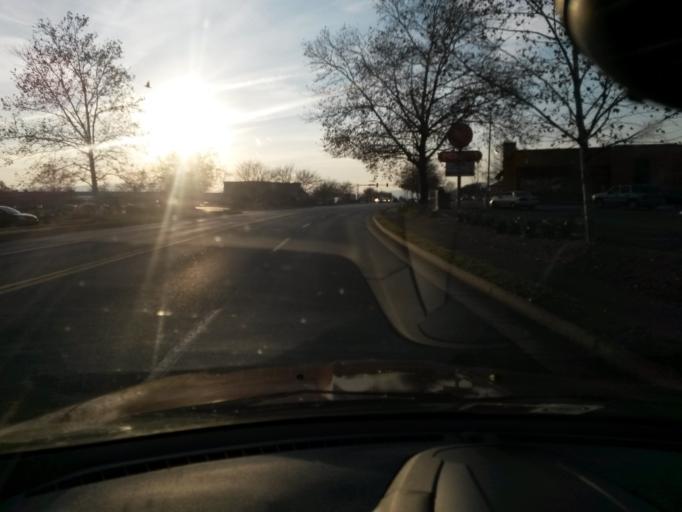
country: US
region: Virginia
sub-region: Roanoke County
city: Hollins
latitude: 37.3189
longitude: -79.9618
